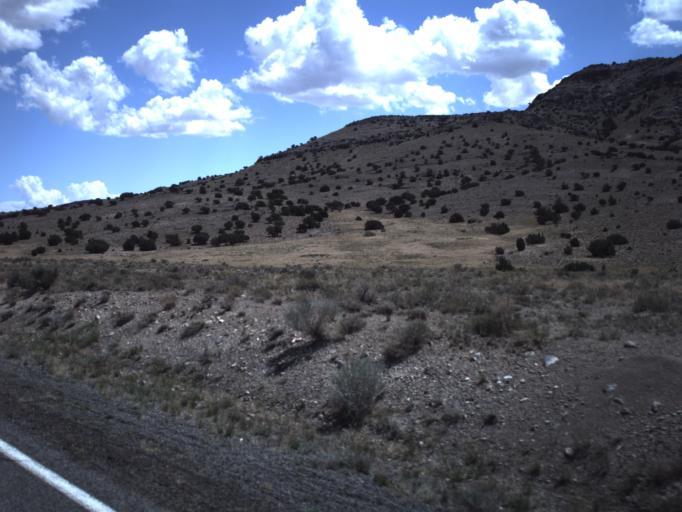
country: US
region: Utah
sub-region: Beaver County
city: Milford
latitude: 39.0729
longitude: -113.6441
